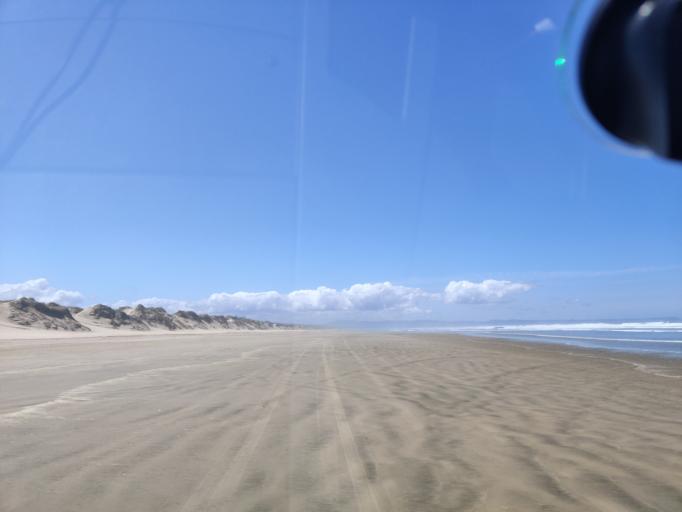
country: NZ
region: Northland
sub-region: Far North District
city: Kaitaia
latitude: -34.9754
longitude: 173.1373
